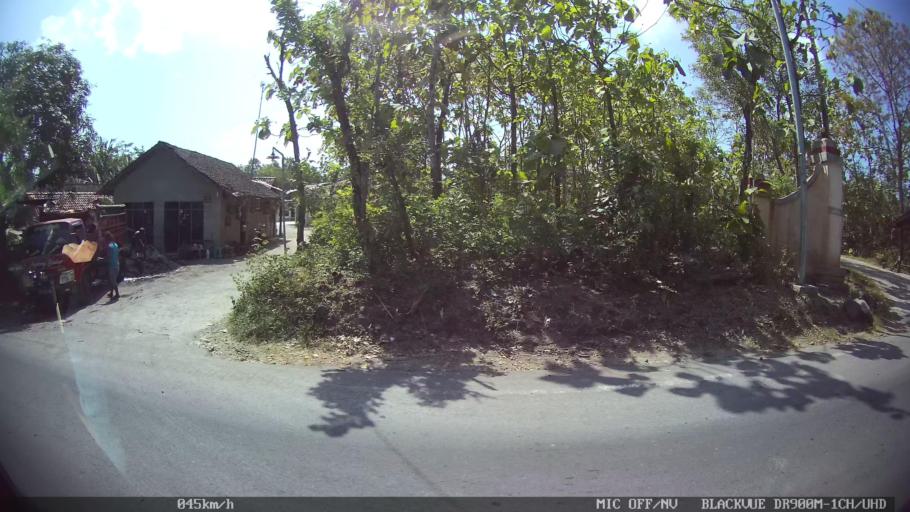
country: ID
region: Daerah Istimewa Yogyakarta
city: Pundong
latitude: -7.9870
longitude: 110.3242
